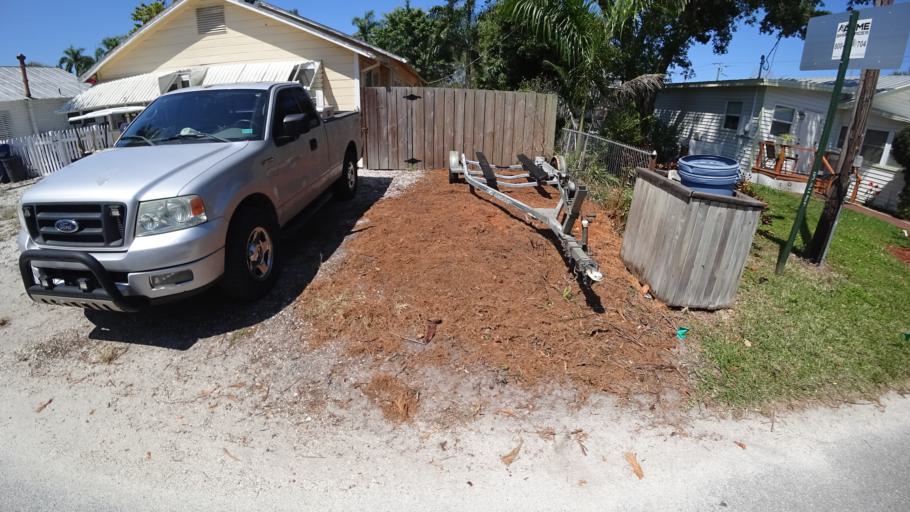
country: US
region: Florida
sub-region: Manatee County
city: Cortez
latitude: 27.4687
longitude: -82.6857
